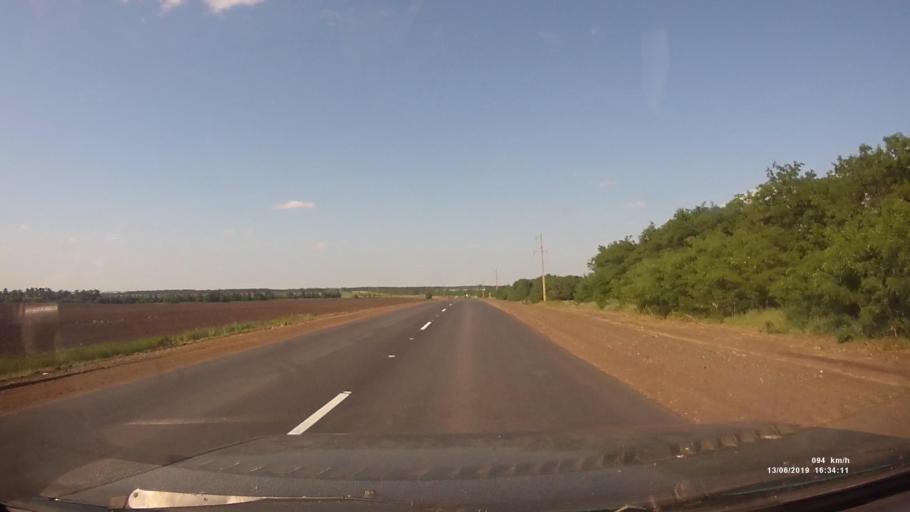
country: RU
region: Rostov
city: Kazanskaya
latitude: 49.8690
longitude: 41.2892
